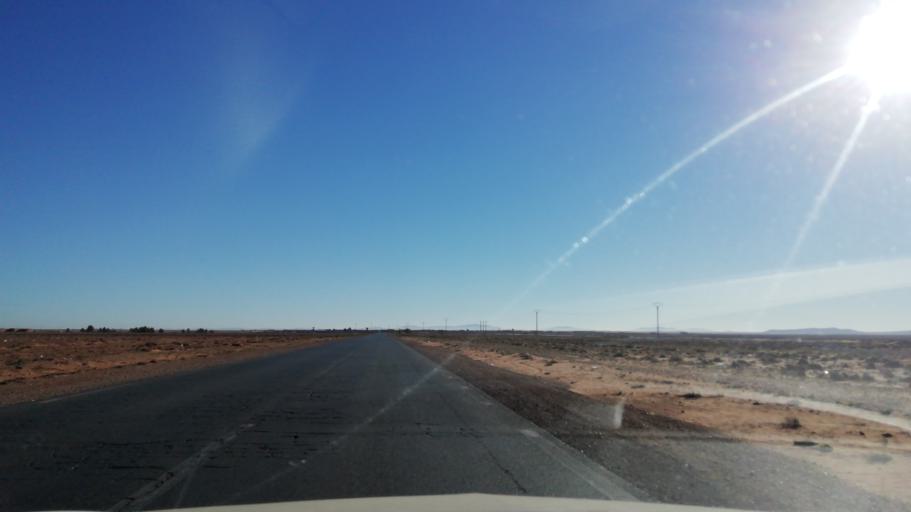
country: DZ
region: El Bayadh
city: El Bayadh
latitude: 33.8547
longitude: 0.6047
